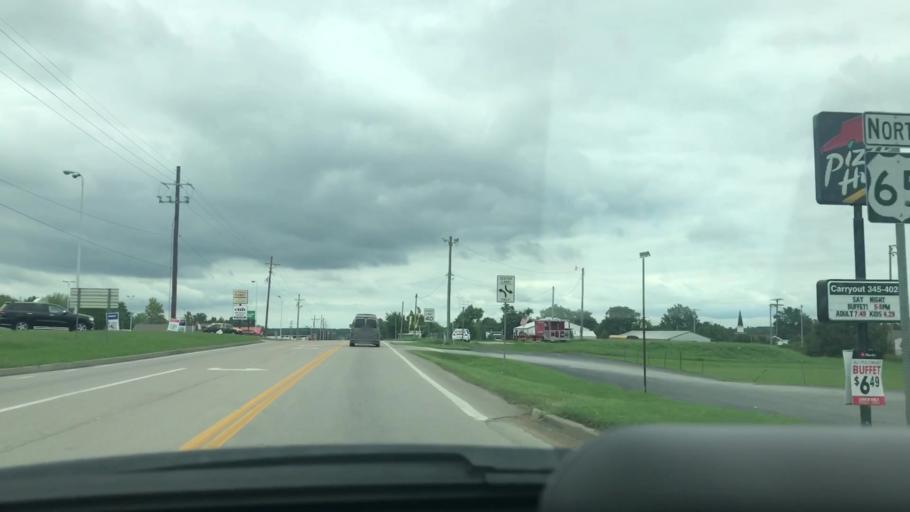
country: US
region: Missouri
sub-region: Dallas County
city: Buffalo
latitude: 37.6410
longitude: -93.1042
